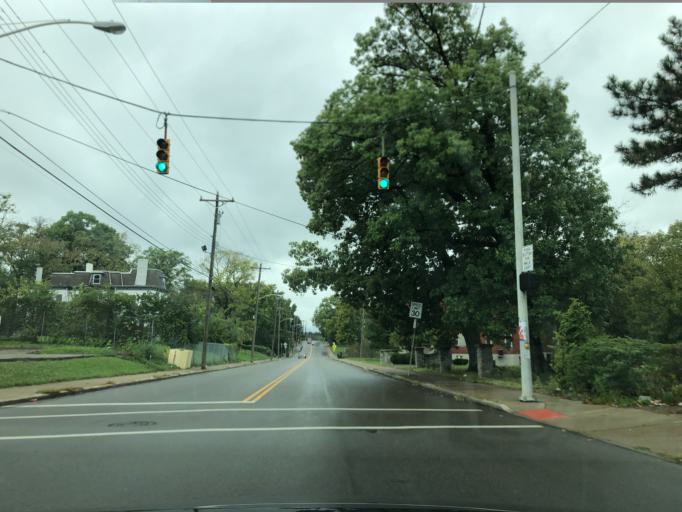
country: US
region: Ohio
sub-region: Hamilton County
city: Saint Bernard
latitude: 39.1463
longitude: -84.4995
